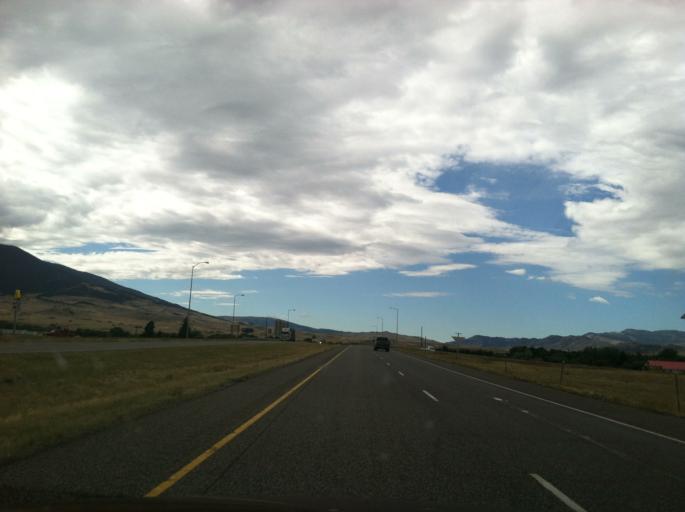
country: US
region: Montana
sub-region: Park County
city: Livingston
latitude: 45.6445
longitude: -110.5711
